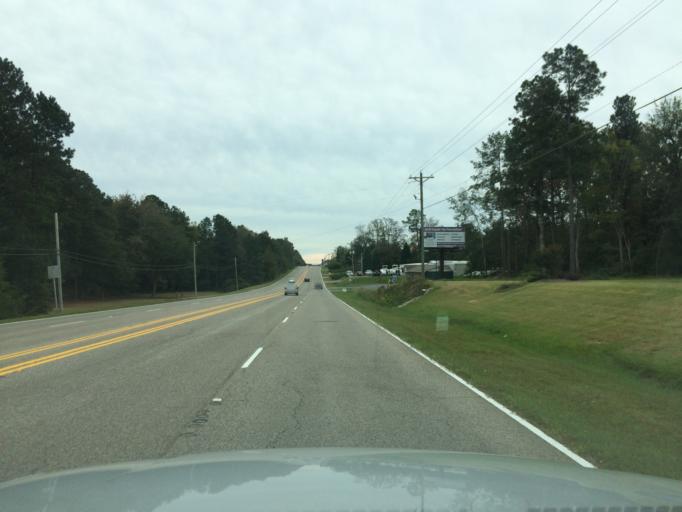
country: US
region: South Carolina
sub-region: Aiken County
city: New Ellenton
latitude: 33.4319
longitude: -81.6860
